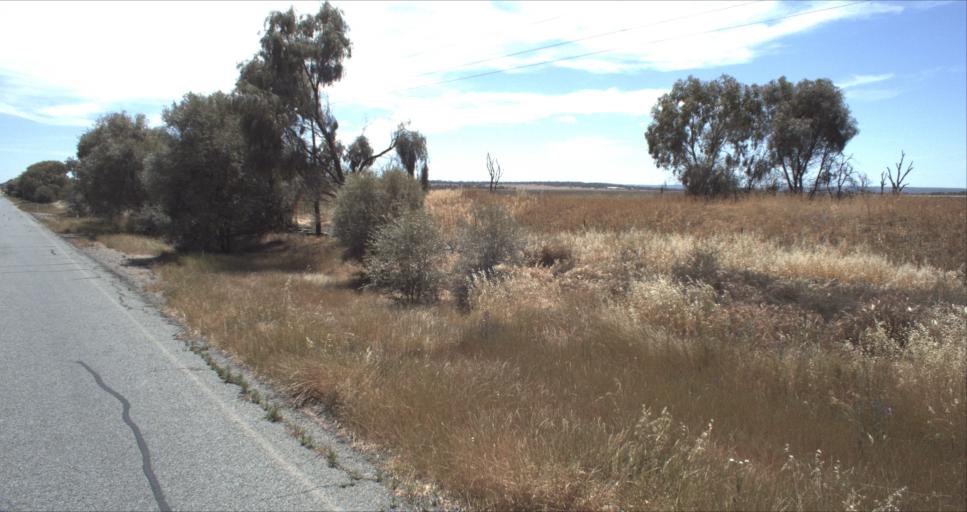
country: AU
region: New South Wales
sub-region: Leeton
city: Leeton
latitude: -34.6383
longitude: 146.4638
